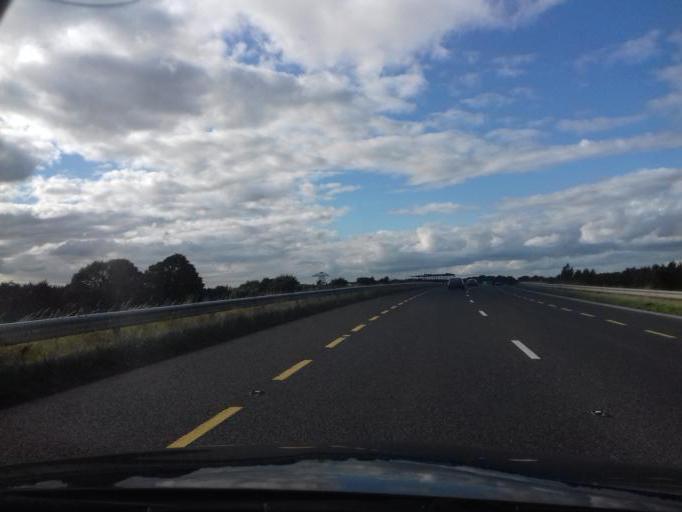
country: IE
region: Leinster
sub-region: Uibh Fhaili
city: Tullamore
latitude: 53.2844
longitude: -7.4781
